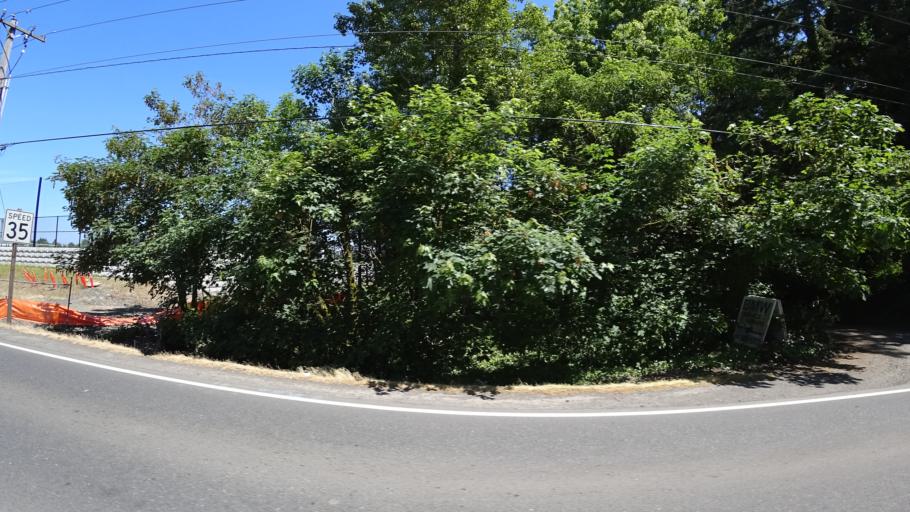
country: US
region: Oregon
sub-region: Multnomah County
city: Gresham
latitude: 45.4872
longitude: -122.4847
